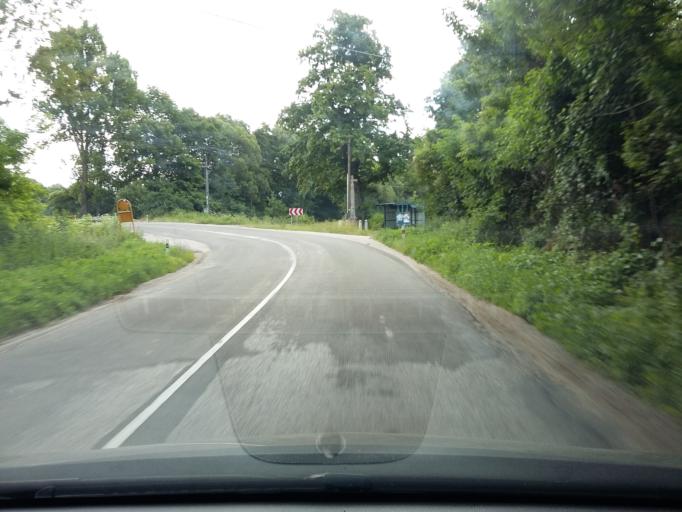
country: SK
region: Trnavsky
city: Smolenice
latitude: 48.5367
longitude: 17.4416
